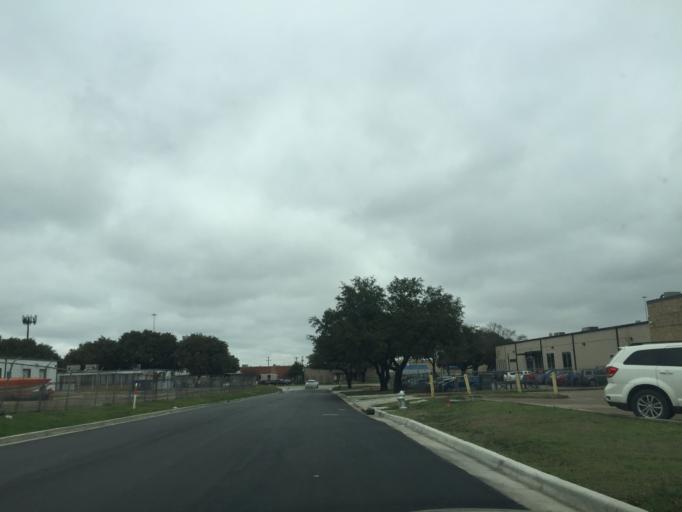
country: US
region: Texas
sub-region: Dallas County
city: Grand Prairie
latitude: 32.7550
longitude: -97.0515
